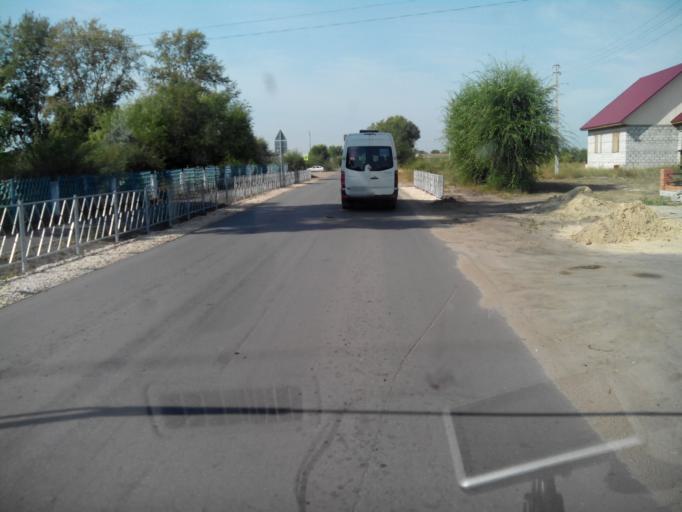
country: RU
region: Samara
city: Balasheyka
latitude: 53.1539
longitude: 48.1068
